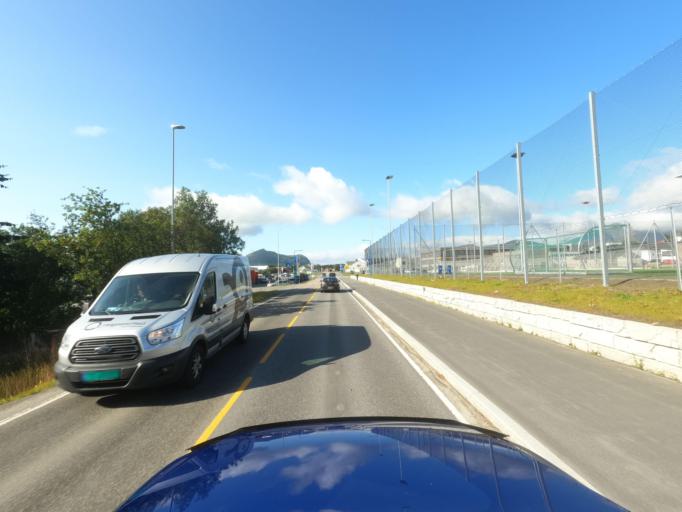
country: NO
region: Nordland
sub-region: Vestvagoy
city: Leknes
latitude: 68.1444
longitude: 13.6243
